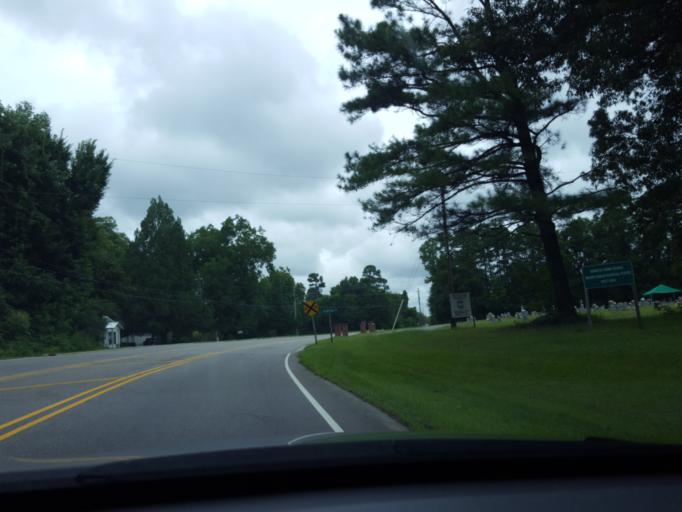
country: US
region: North Carolina
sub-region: Martin County
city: Williamston
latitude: 35.8028
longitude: -76.9011
